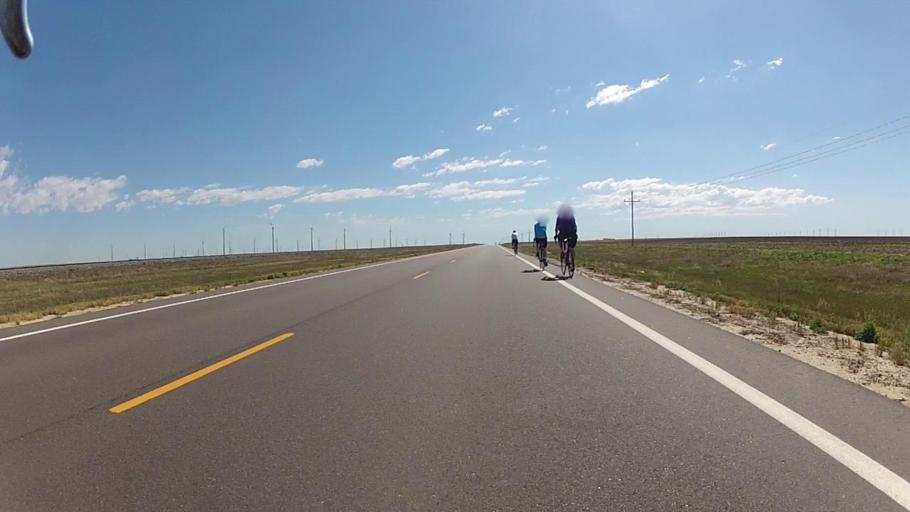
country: US
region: Kansas
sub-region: Gray County
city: Cimarron
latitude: 37.6050
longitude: -100.4223
